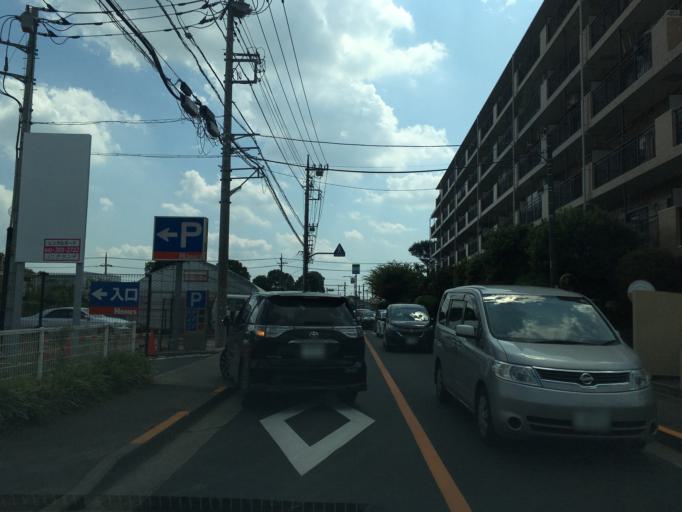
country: JP
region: Tokyo
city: Higashimurayama-shi
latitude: 35.7682
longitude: 139.4858
